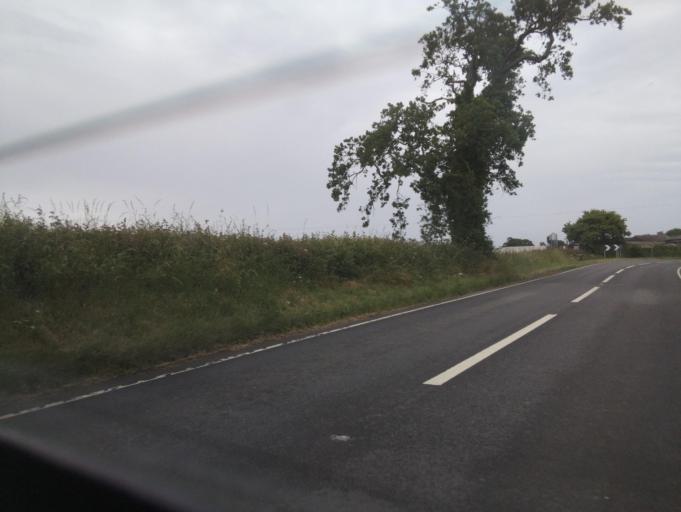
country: GB
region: England
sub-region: Devon
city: Colyton
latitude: 50.7448
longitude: -3.0373
